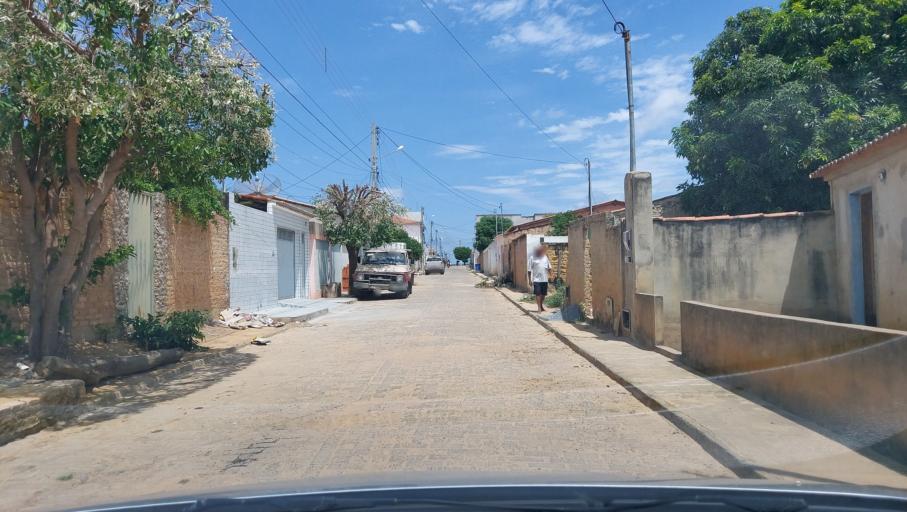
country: BR
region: Bahia
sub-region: Oliveira Dos Brejinhos
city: Beira Rio
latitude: -12.0021
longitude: -42.6277
